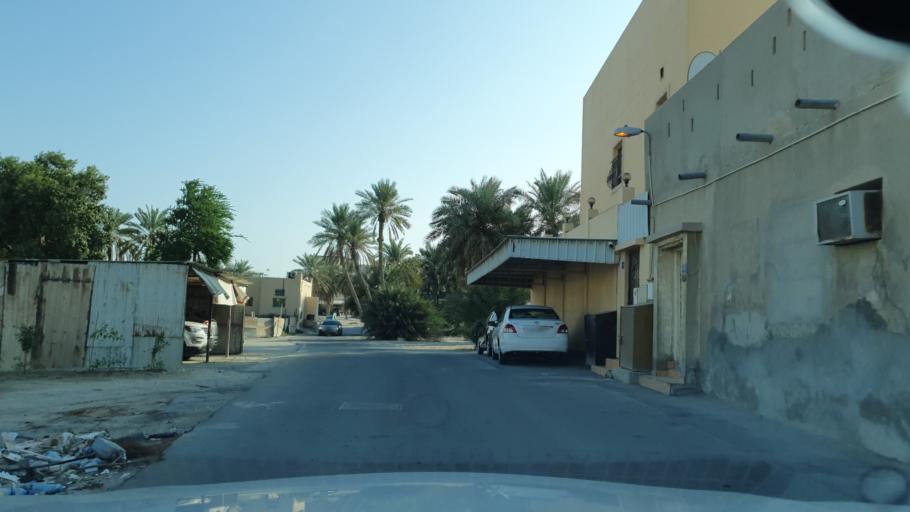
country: BH
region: Manama
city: Jidd Hafs
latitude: 26.2206
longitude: 50.4636
